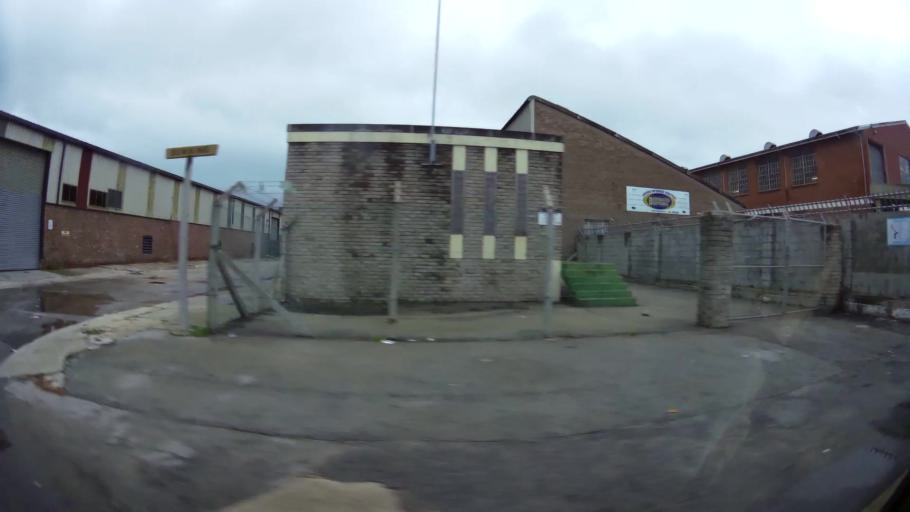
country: ZA
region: Eastern Cape
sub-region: Nelson Mandela Bay Metropolitan Municipality
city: Port Elizabeth
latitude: -33.9416
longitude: 25.6084
